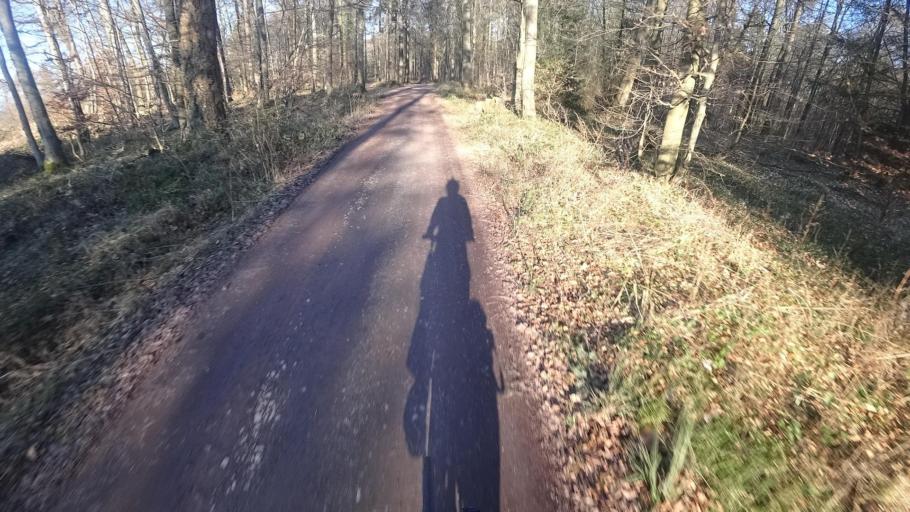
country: DE
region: Rheinland-Pfalz
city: Waldesch
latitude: 50.2627
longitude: 7.5318
